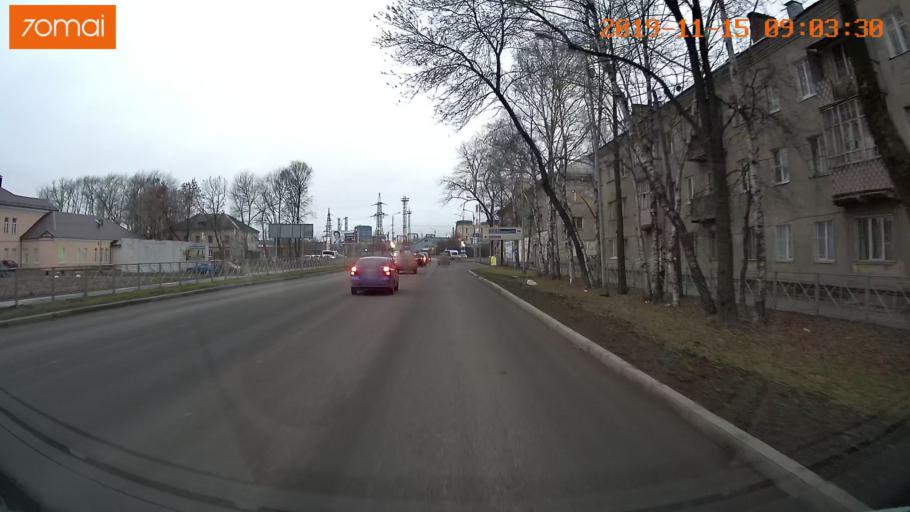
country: RU
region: Vologda
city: Cherepovets
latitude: 59.1388
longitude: 37.9209
